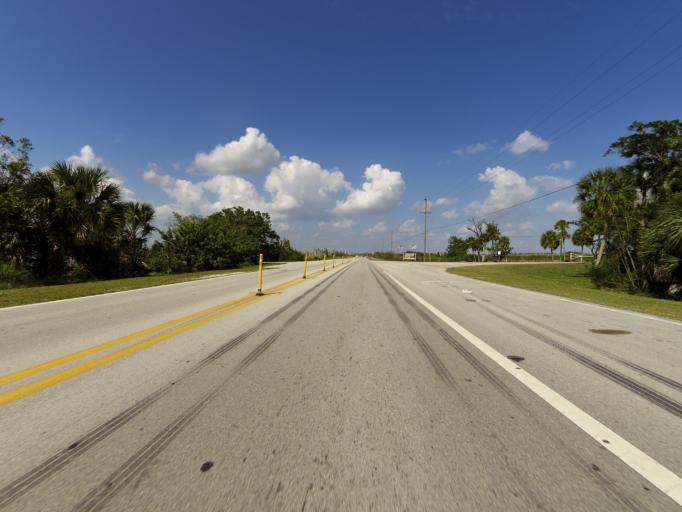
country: US
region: Florida
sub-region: Miami-Dade County
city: Palm Springs North
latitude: 25.9260
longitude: -80.4535
